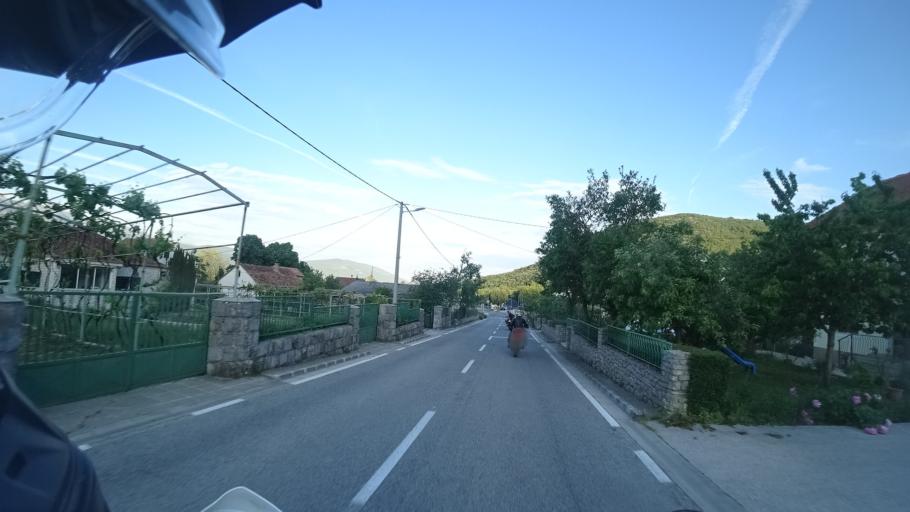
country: HR
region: Sibensko-Kniniska
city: Knin
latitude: 43.9067
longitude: 16.4043
